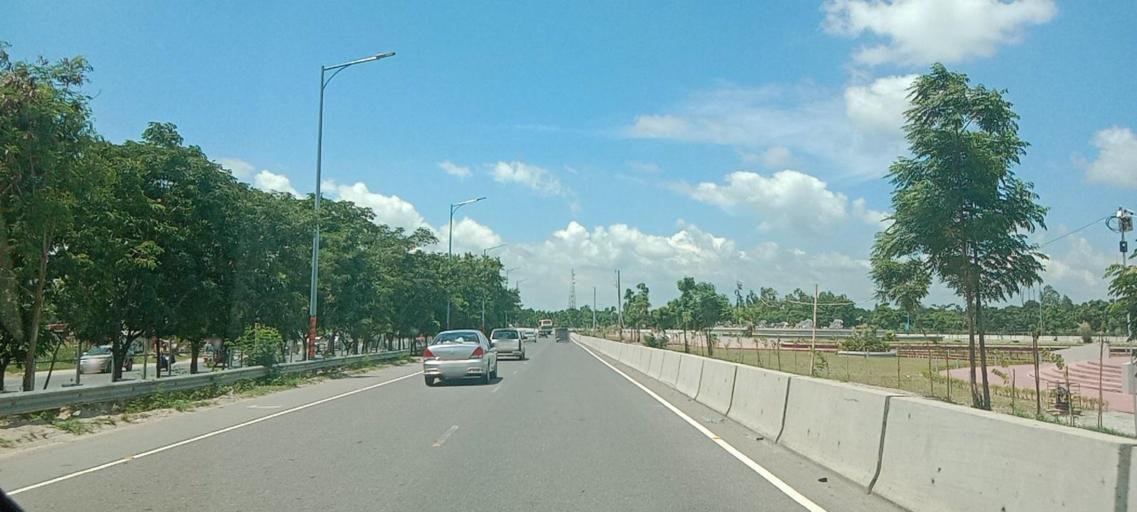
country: BD
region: Dhaka
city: Dohar
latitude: 23.4784
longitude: 90.2663
